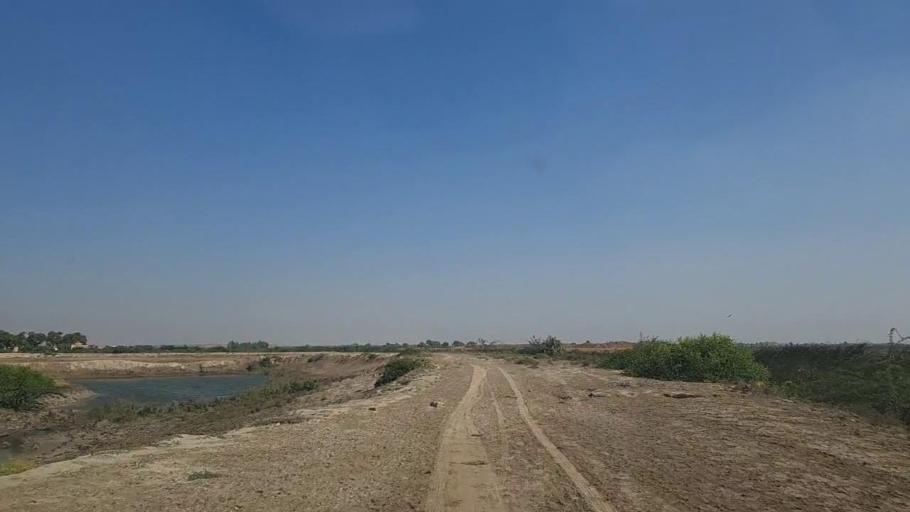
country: PK
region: Sindh
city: Thatta
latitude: 24.8069
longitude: 67.9863
